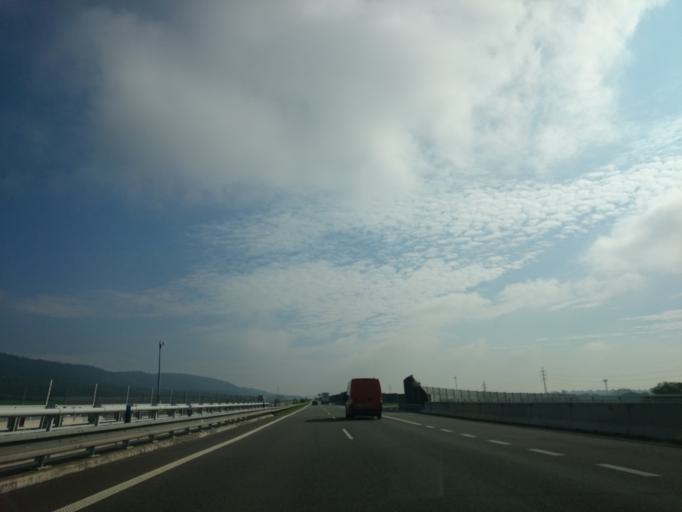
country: CZ
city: Odry
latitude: 49.6396
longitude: 17.8658
